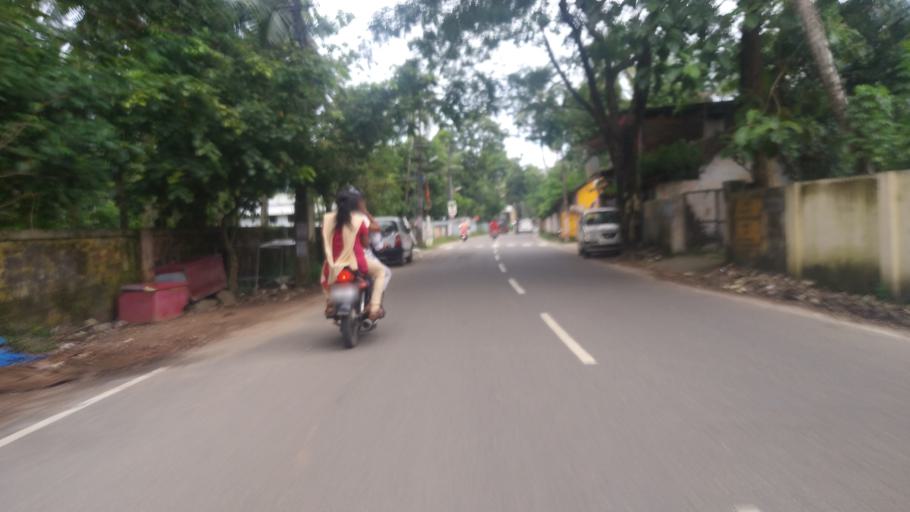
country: IN
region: Kerala
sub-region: Alappuzha
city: Arukutti
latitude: 9.8678
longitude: 76.2913
